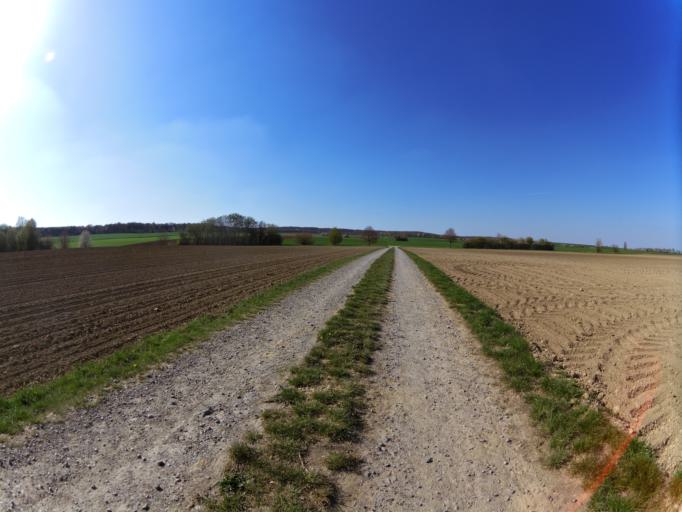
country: DE
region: Bavaria
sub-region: Regierungsbezirk Unterfranken
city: Kurnach
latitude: 49.8656
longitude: 10.0080
